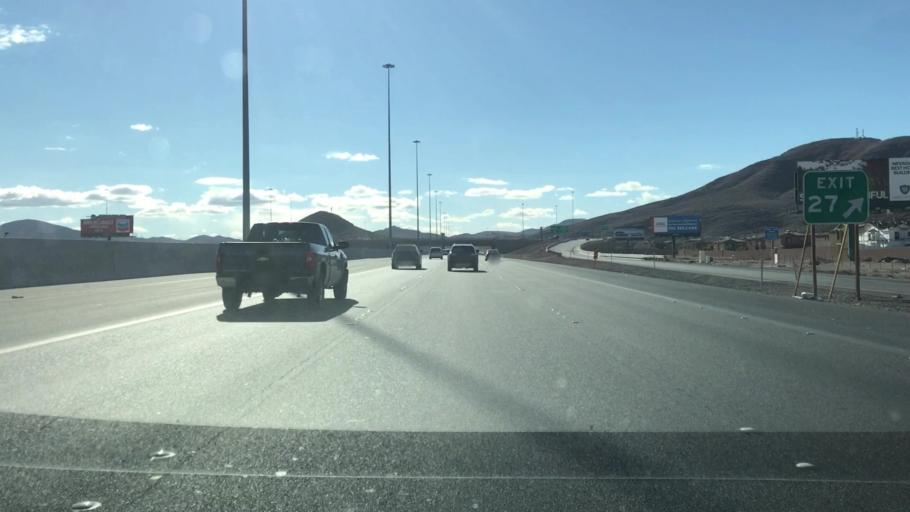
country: US
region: Nevada
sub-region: Clark County
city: Enterprise
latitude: 35.9684
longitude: -115.1818
